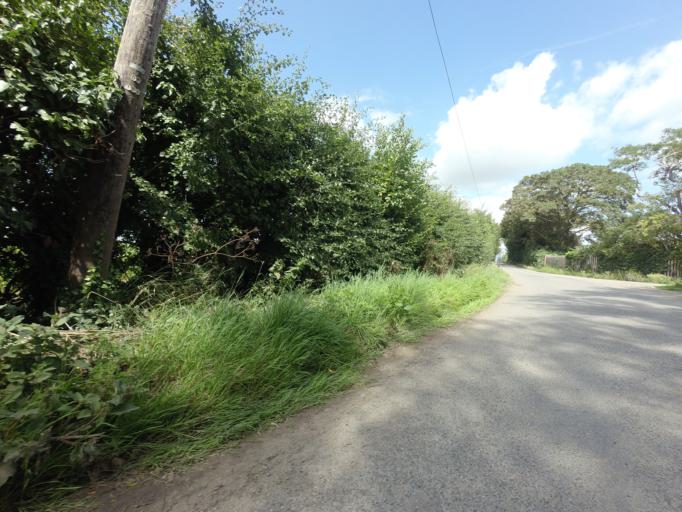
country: GB
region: England
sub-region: Kent
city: Stone
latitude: 50.9938
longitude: 0.8060
